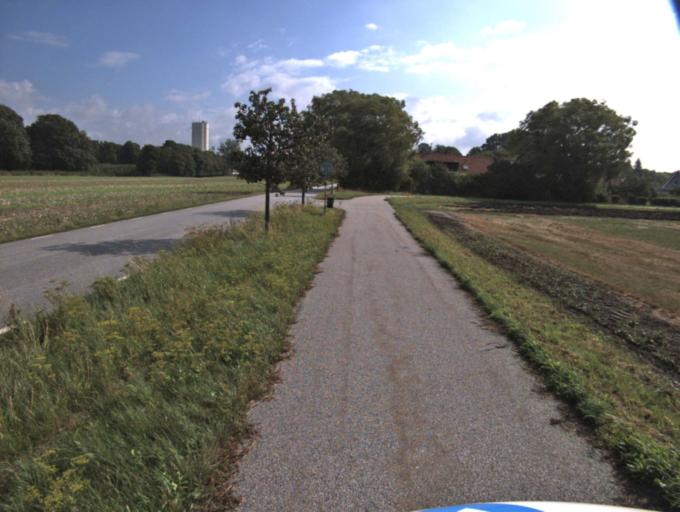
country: SE
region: Skane
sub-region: Kavlinge Kommun
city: Hofterup
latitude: 55.7730
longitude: 12.9485
